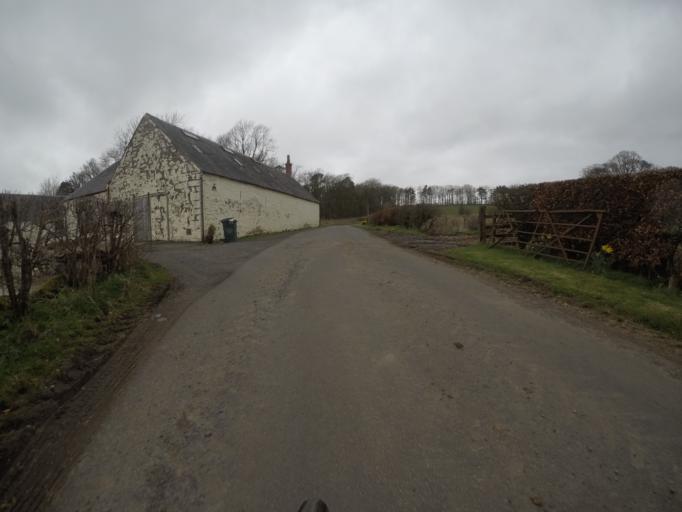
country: GB
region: Scotland
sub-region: East Ayrshire
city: Galston
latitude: 55.6213
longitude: -4.3551
